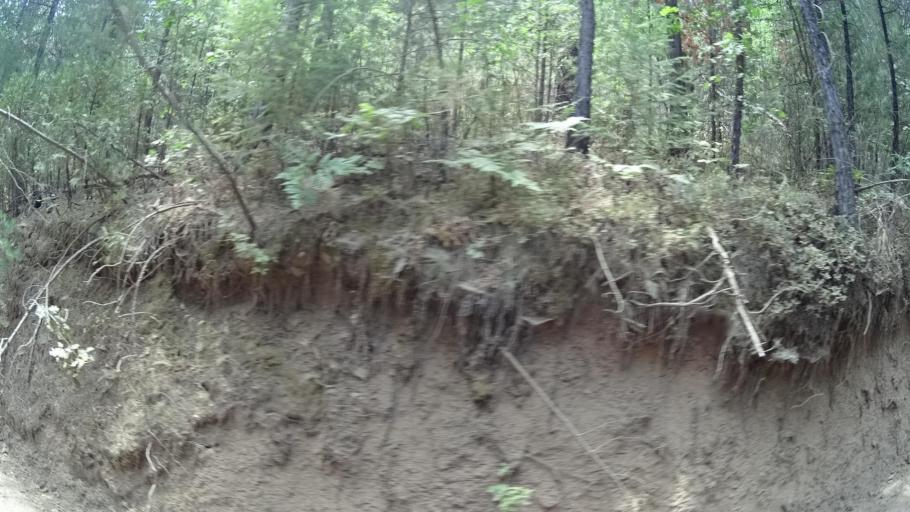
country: US
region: California
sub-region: Mariposa County
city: Midpines
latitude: 37.7519
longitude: -120.0528
